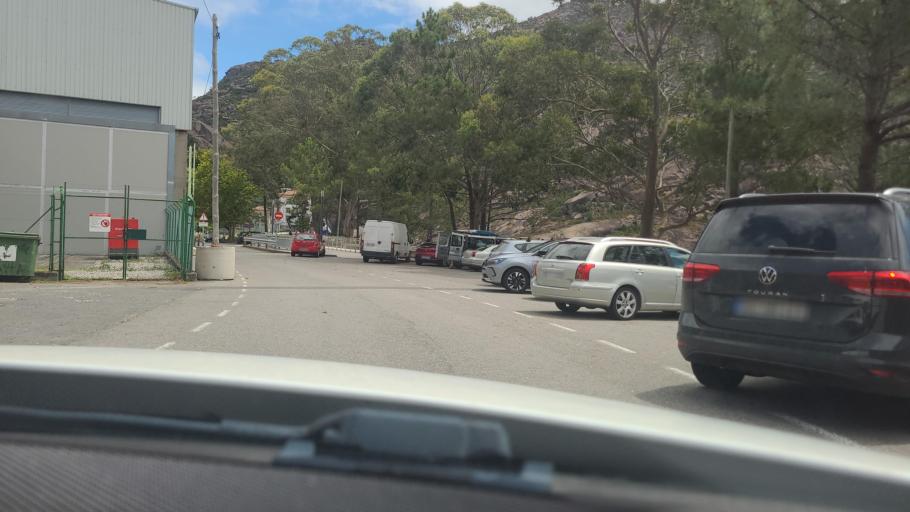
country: ES
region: Galicia
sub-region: Provincia da Coruna
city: Corcubion
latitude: 42.9126
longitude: -9.1230
